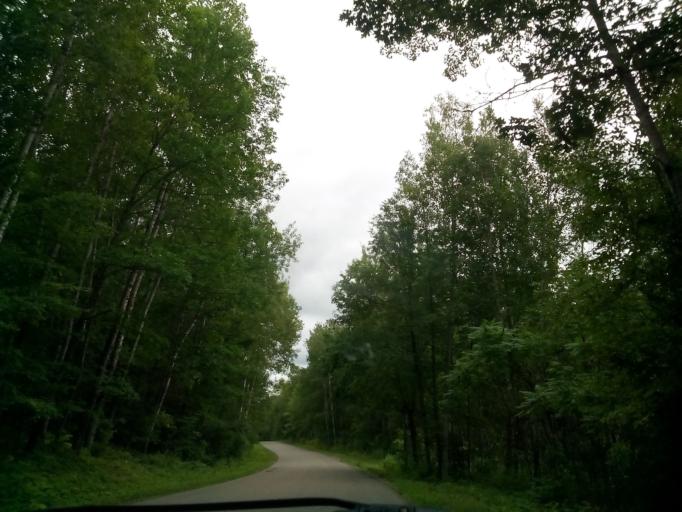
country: US
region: Wisconsin
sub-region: Menominee County
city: Legend Lake
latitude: 45.3216
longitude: -88.5262
